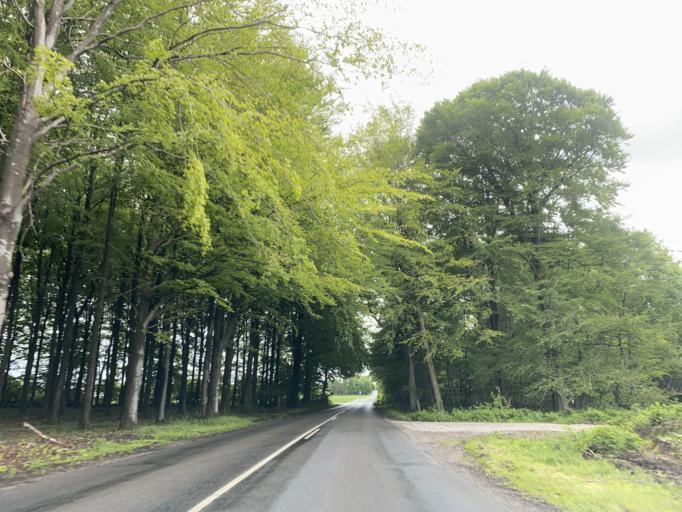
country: DK
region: Central Jutland
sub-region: Favrskov Kommune
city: Hammel
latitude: 56.2581
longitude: 9.9525
